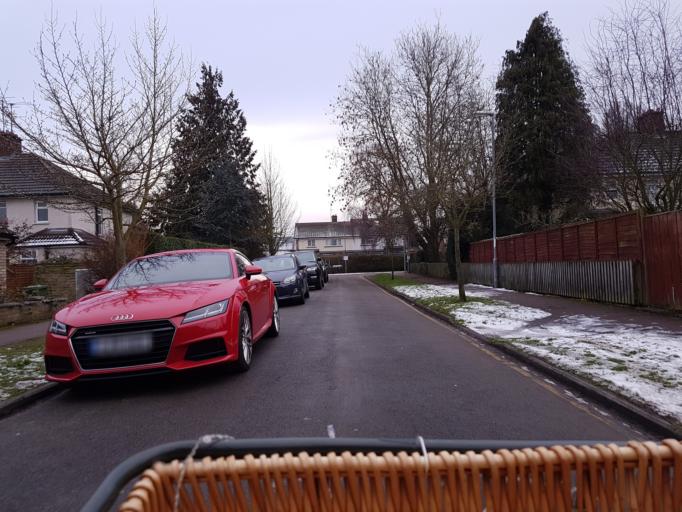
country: GB
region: England
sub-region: Cambridgeshire
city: Cambridge
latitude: 52.1831
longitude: 0.1454
